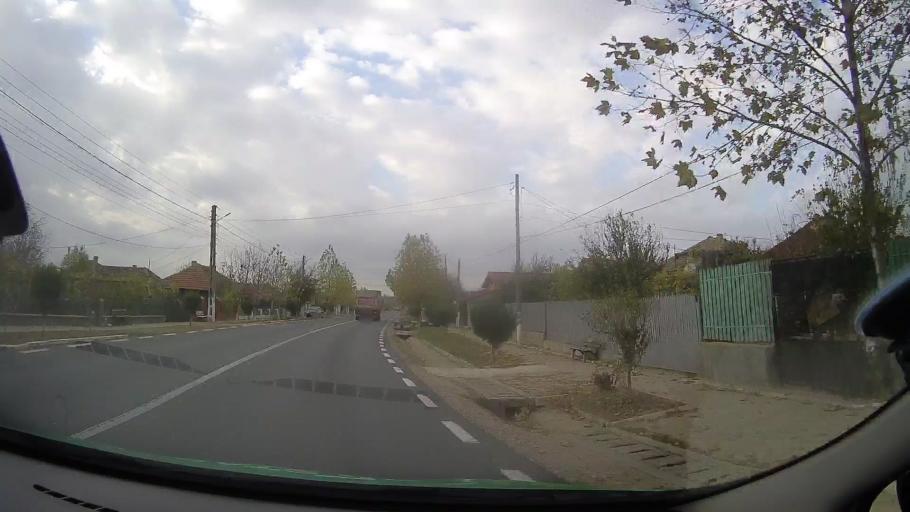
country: RO
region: Constanta
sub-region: Comuna Mircea Voda
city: Satu Nou
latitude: 44.2661
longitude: 28.2308
